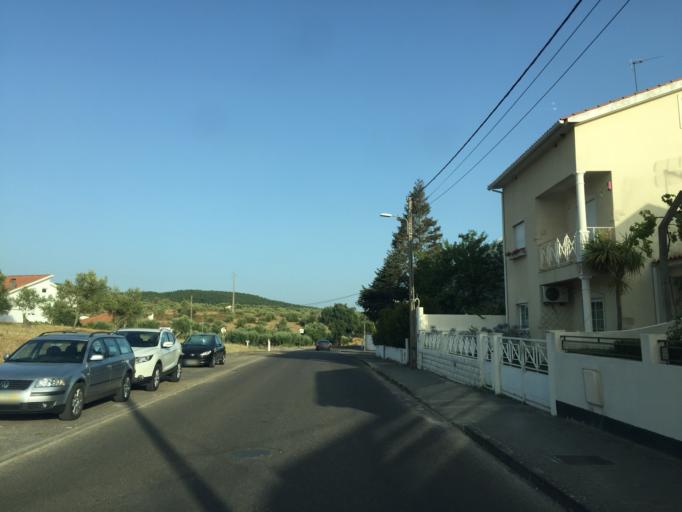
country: PT
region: Santarem
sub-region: Chamusca
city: Vila Nova da Barquinha
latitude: 39.4670
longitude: -8.4397
